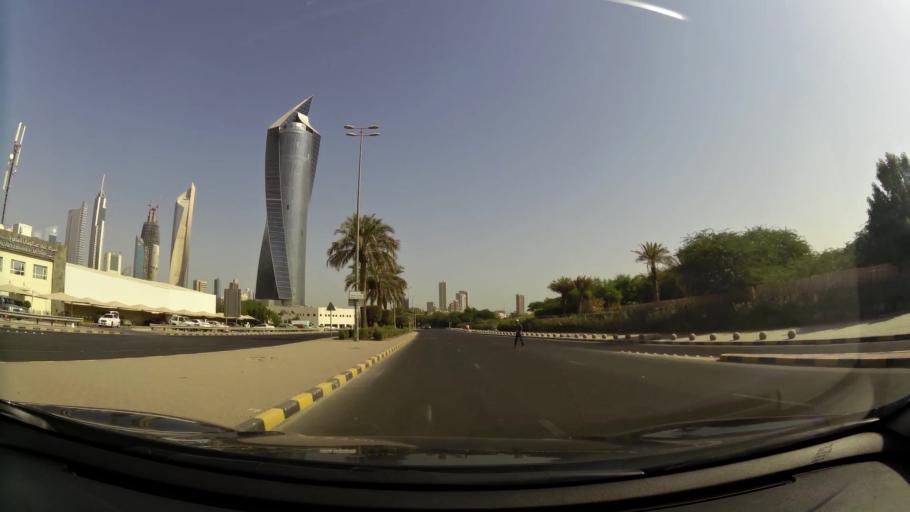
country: KW
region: Al Asimah
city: Ad Dasmah
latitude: 29.3670
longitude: 47.9909
